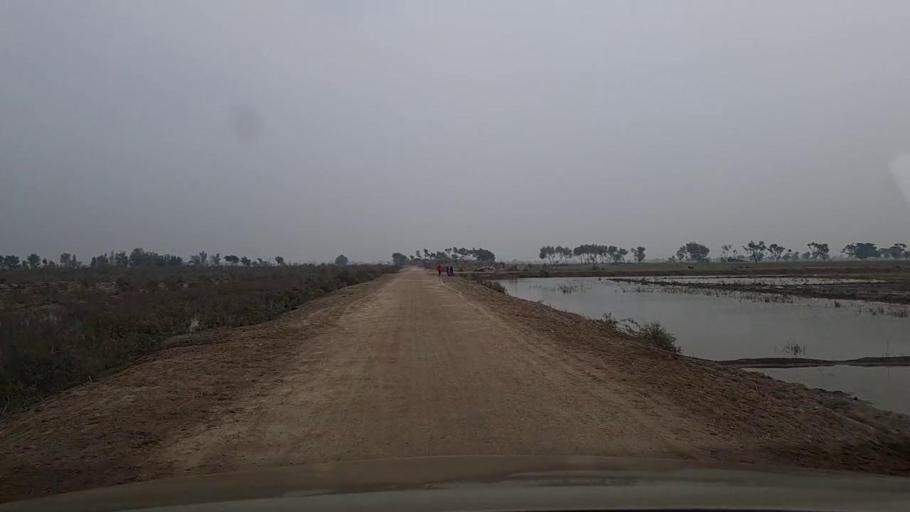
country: PK
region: Sindh
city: Sanghar
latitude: 26.1190
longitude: 68.9191
